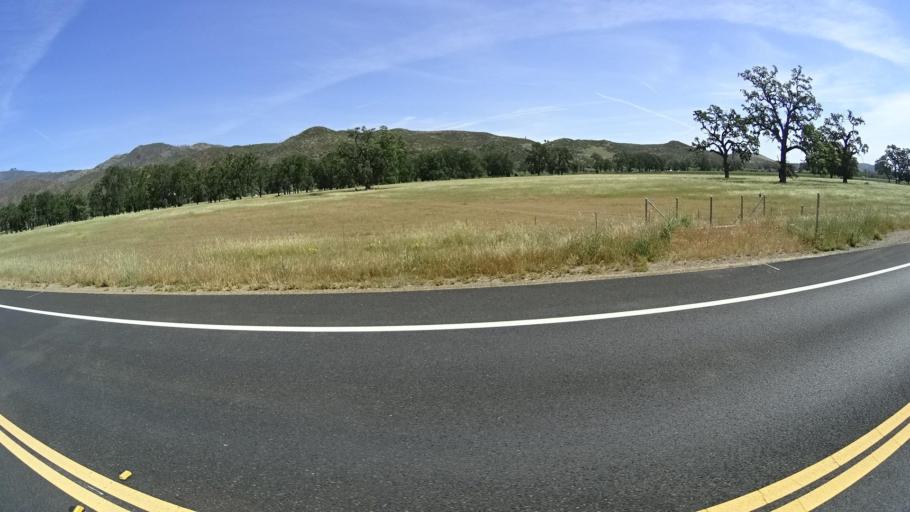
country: US
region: California
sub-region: Lake County
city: Middletown
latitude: 38.7630
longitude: -122.6444
